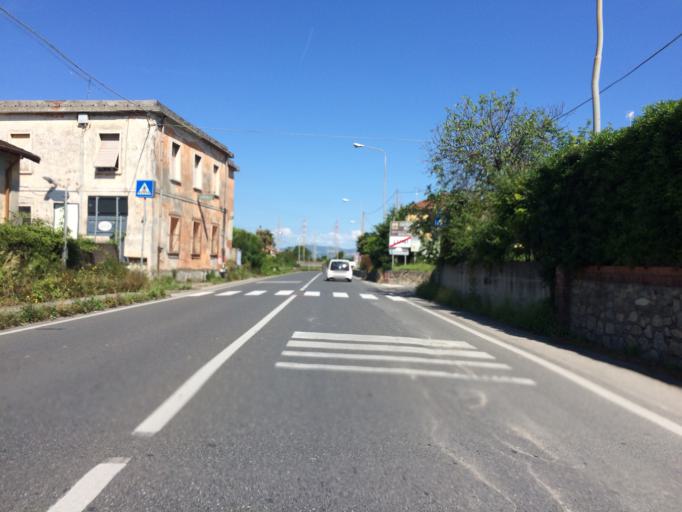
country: IT
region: Liguria
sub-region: Provincia di La Spezia
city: Colombiera-Molicciara
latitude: 44.0747
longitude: 10.0165
